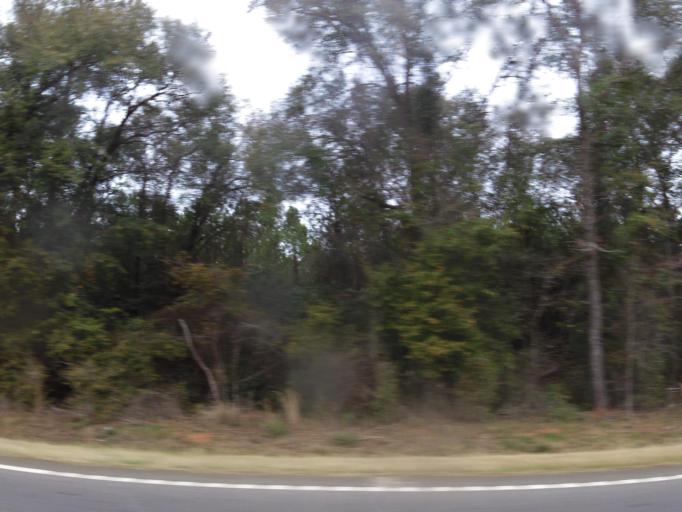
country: US
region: Georgia
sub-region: Randolph County
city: Shellman
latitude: 31.7762
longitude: -84.5732
